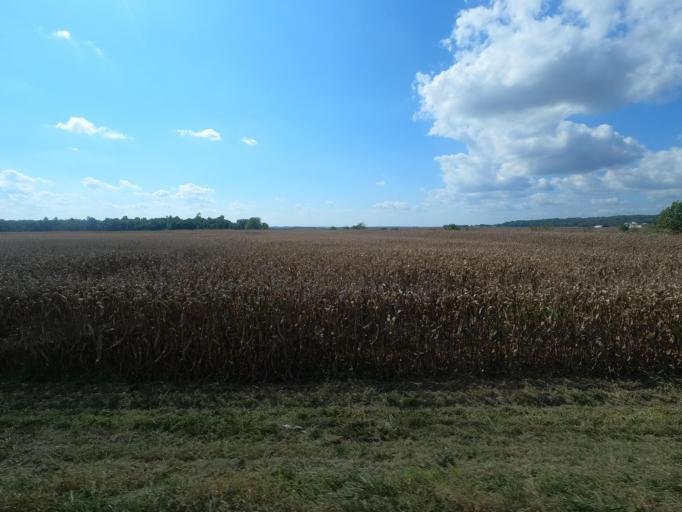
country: US
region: Illinois
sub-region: Massac County
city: Metropolis
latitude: 37.2810
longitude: -88.7576
